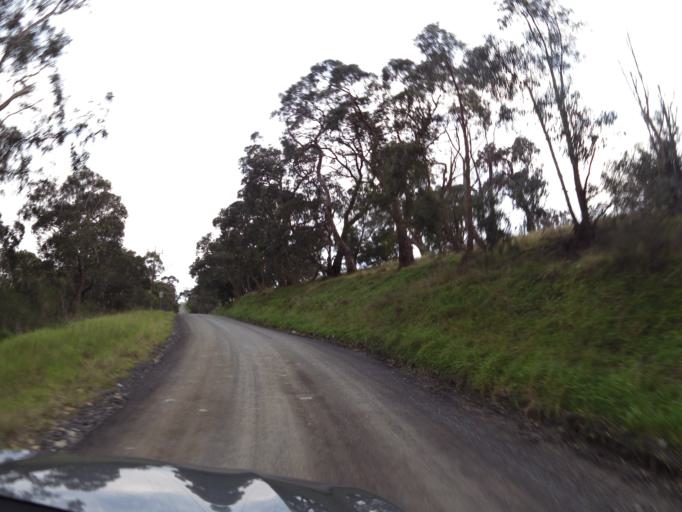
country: AU
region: Victoria
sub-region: Knox
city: Ferntree Gully
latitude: -37.9038
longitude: 145.3075
